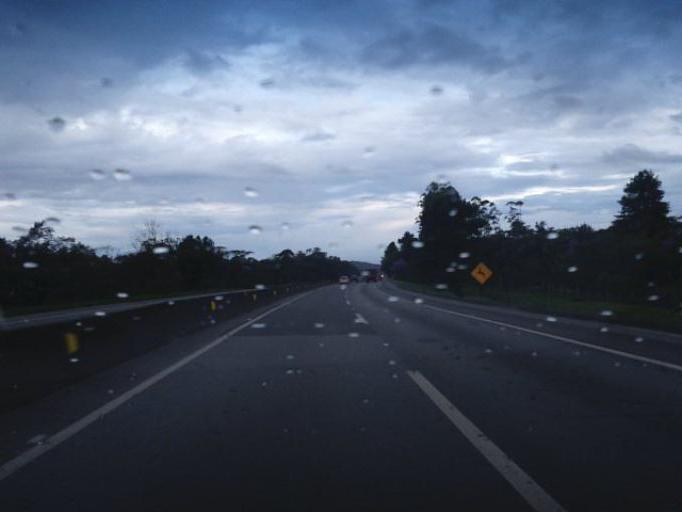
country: BR
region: Santa Catarina
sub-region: Joinville
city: Joinville
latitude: -26.0406
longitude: -48.8597
